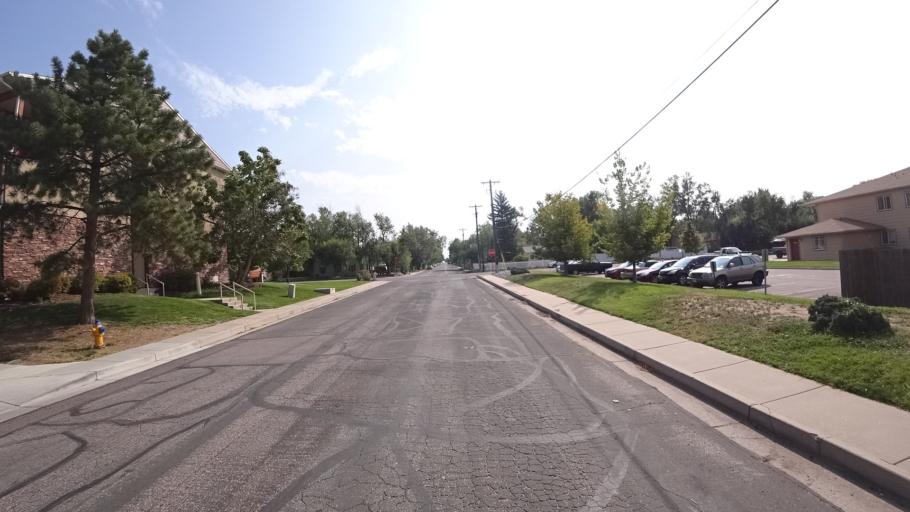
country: US
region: Colorado
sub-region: El Paso County
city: Colorado Springs
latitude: 38.8434
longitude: -104.7833
